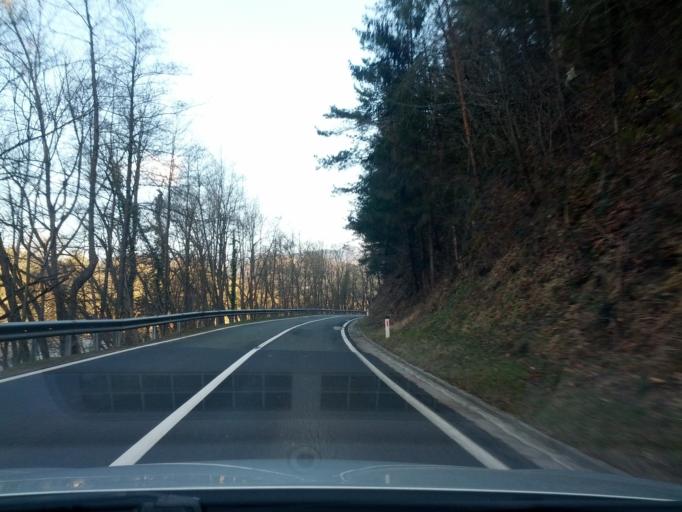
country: SI
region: Smartno pri Litiji
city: Smartno pri Litiji
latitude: 46.0688
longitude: 14.8623
